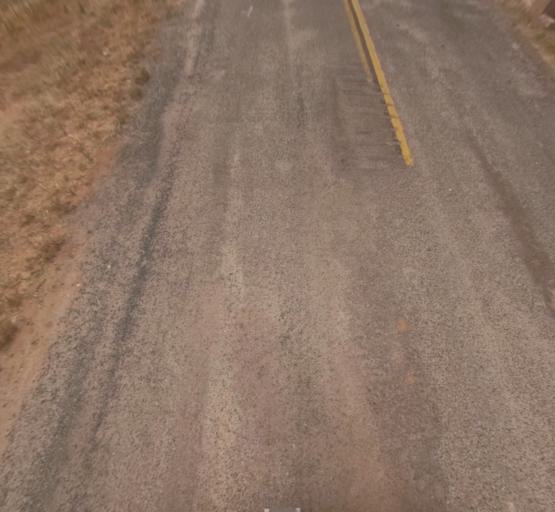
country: US
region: California
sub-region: Madera County
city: Madera Acres
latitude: 37.0188
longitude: -120.0720
